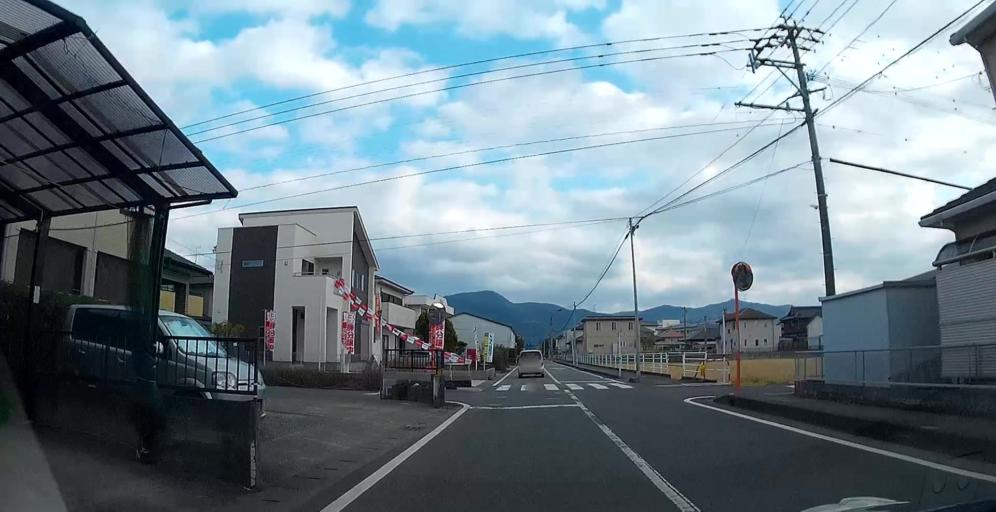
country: JP
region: Kumamoto
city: Yatsushiro
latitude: 32.5381
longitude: 130.6287
